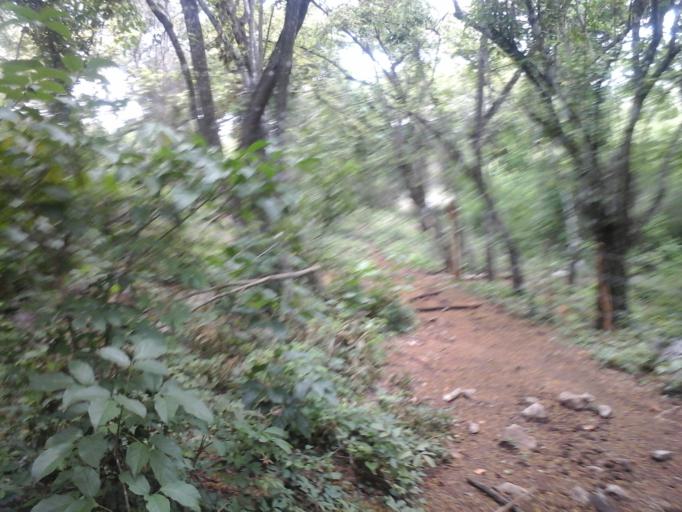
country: CO
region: Cesar
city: Becerril
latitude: 9.7498
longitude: -73.1572
